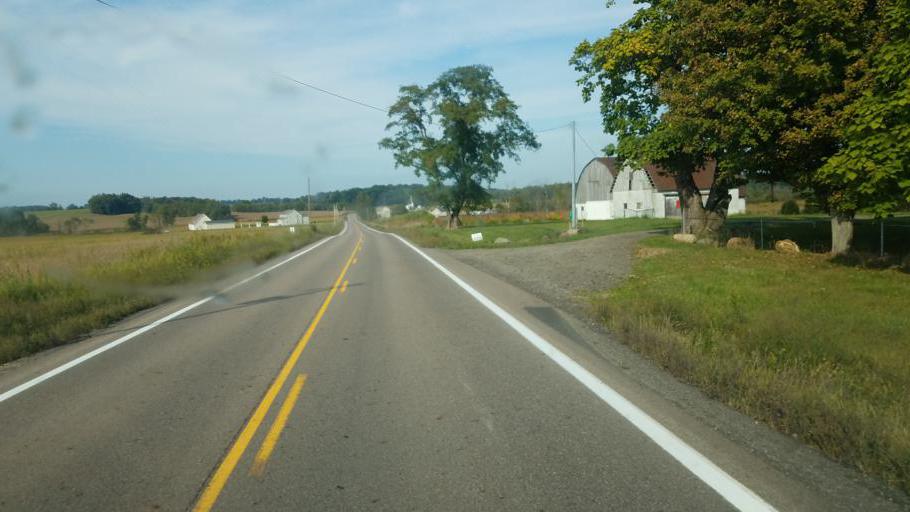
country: US
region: Ohio
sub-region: Knox County
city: Gambier
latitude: 40.3001
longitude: -82.3332
